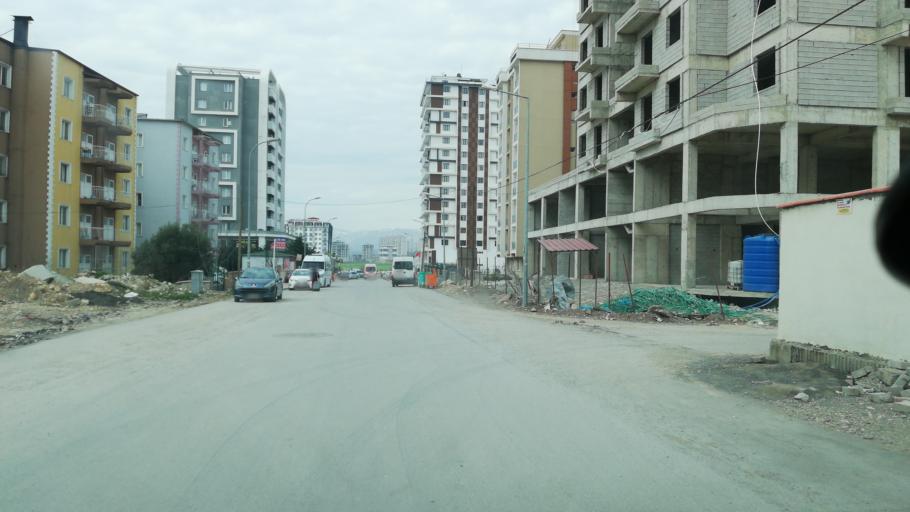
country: TR
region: Kahramanmaras
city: Kahramanmaras
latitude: 37.5885
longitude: 36.8387
